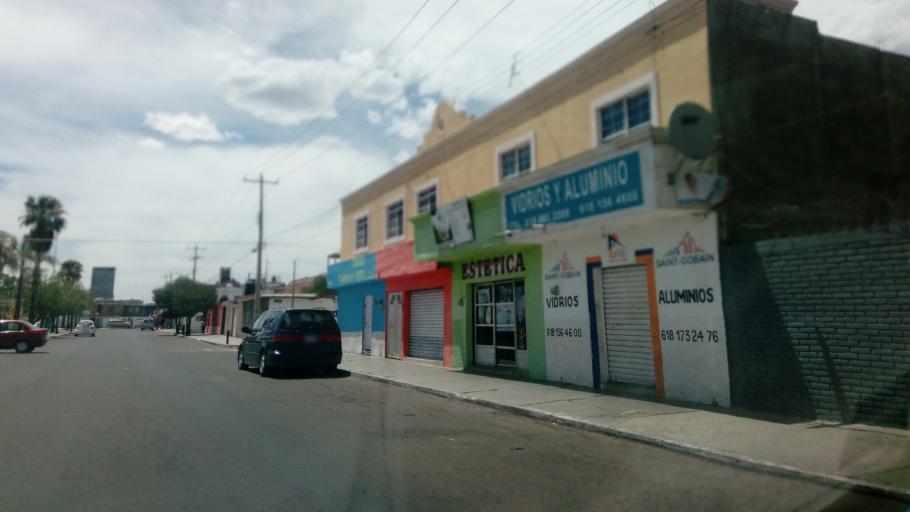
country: MX
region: Durango
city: Victoria de Durango
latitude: 23.9973
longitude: -104.6739
